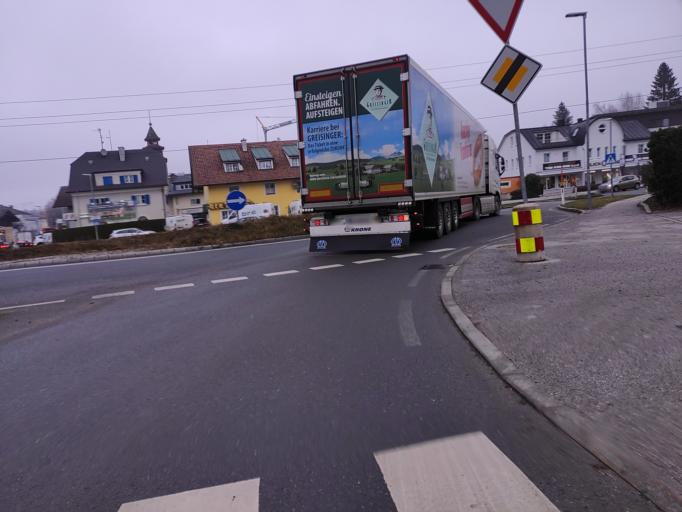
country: AT
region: Salzburg
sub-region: Politischer Bezirk Salzburg-Umgebung
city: Strasswalchen
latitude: 47.9765
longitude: 13.2529
